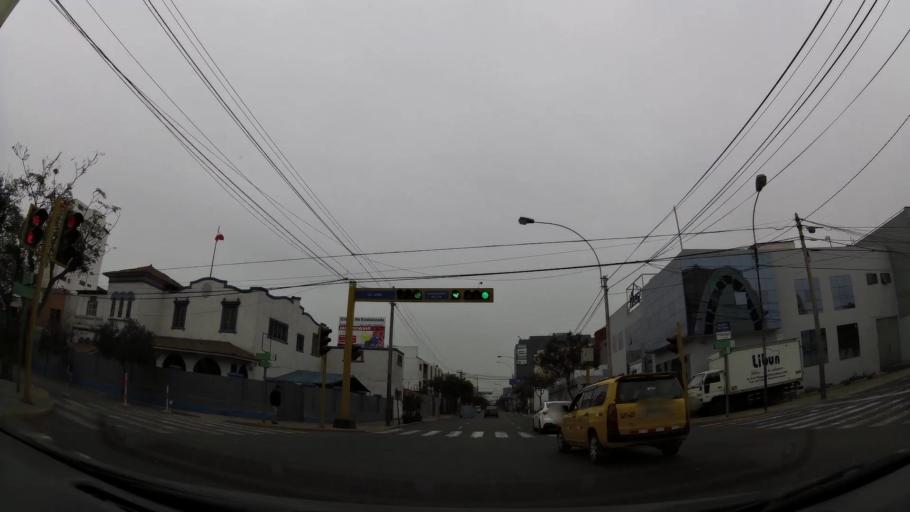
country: PE
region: Lima
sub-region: Lima
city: San Isidro
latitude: -12.1106
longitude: -77.0292
